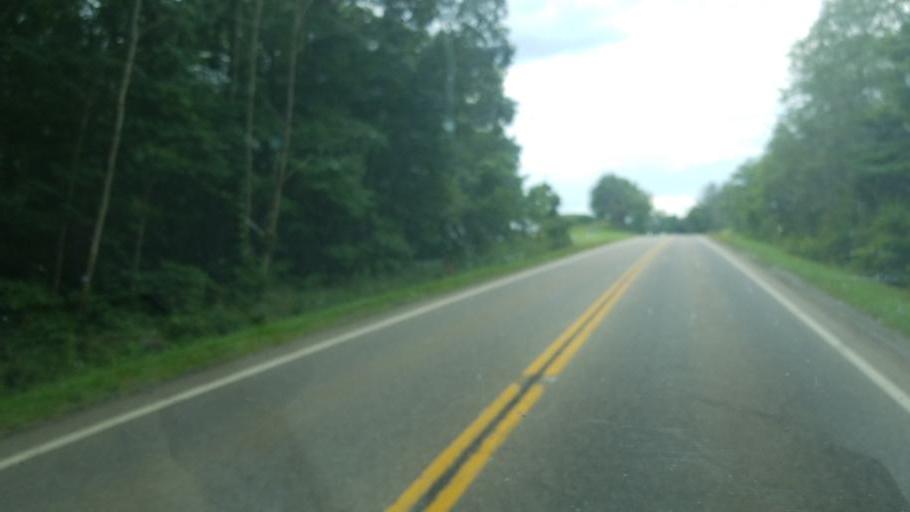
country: US
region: Ohio
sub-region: Carroll County
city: Lake Mohawk
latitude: 40.6446
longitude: -81.3196
